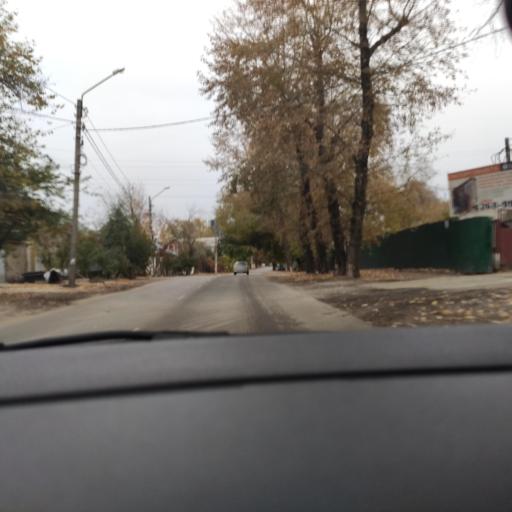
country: RU
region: Voronezj
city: Voronezh
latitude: 51.6641
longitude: 39.1656
